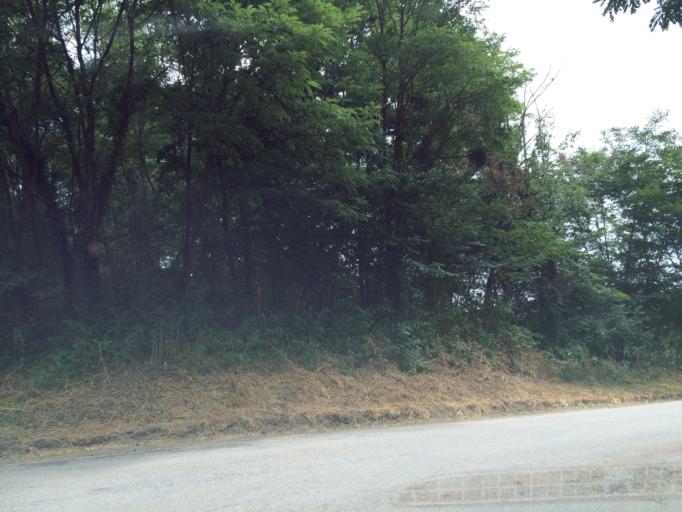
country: FR
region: Bourgogne
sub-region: Departement de l'Yonne
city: Fleury-la-Vallee
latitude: 47.8444
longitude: 3.4116
